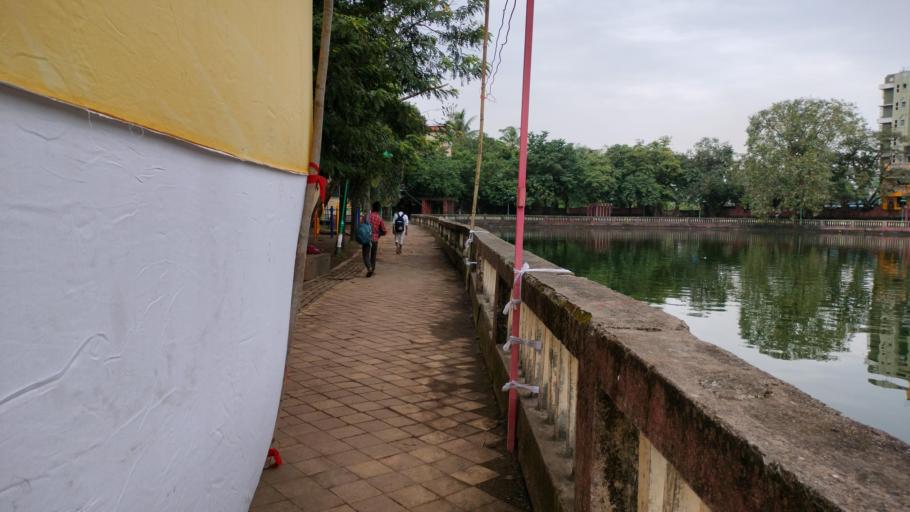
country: IN
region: Maharashtra
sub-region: Thane
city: Virar
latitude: 19.4155
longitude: 72.8617
